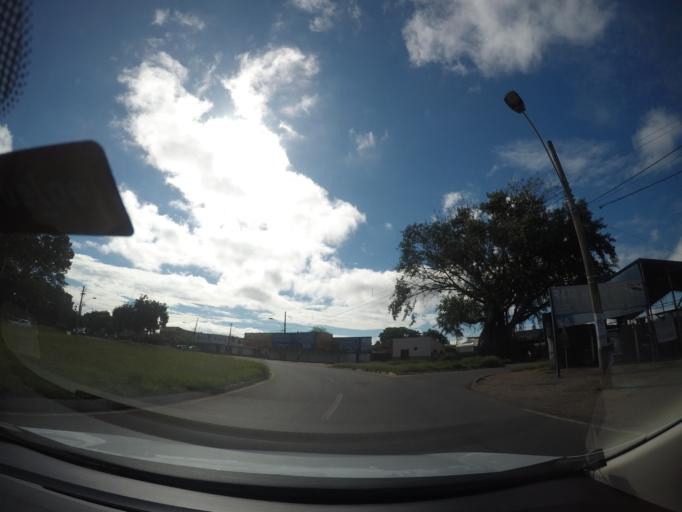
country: BR
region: Goias
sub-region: Goiania
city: Goiania
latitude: -16.6599
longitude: -49.1857
